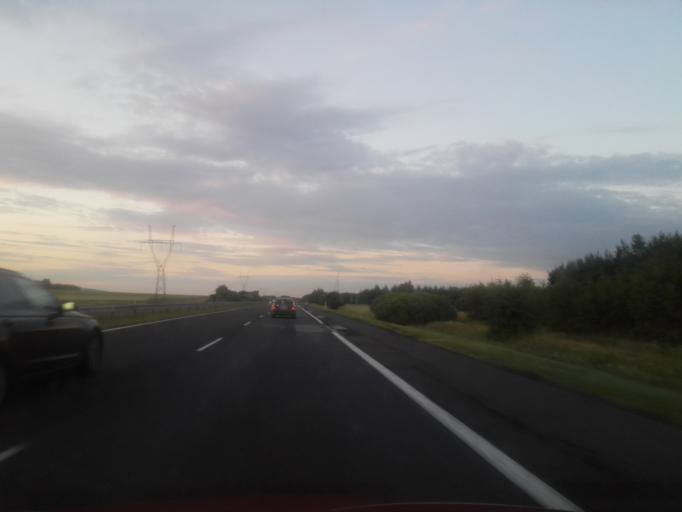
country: PL
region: Lodz Voivodeship
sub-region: Powiat radomszczanski
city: Radomsko
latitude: 51.1236
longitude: 19.4066
